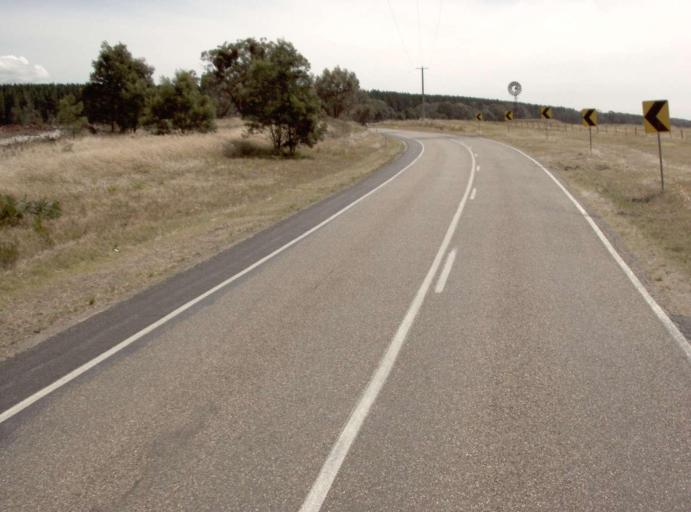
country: AU
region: Victoria
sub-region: Wellington
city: Sale
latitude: -38.1614
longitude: 146.9093
